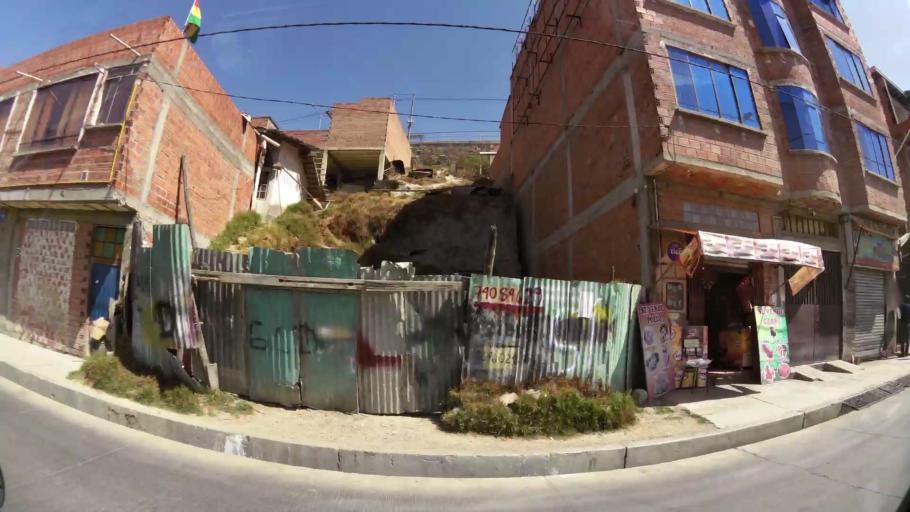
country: BO
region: La Paz
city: La Paz
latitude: -16.5282
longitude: -68.1245
